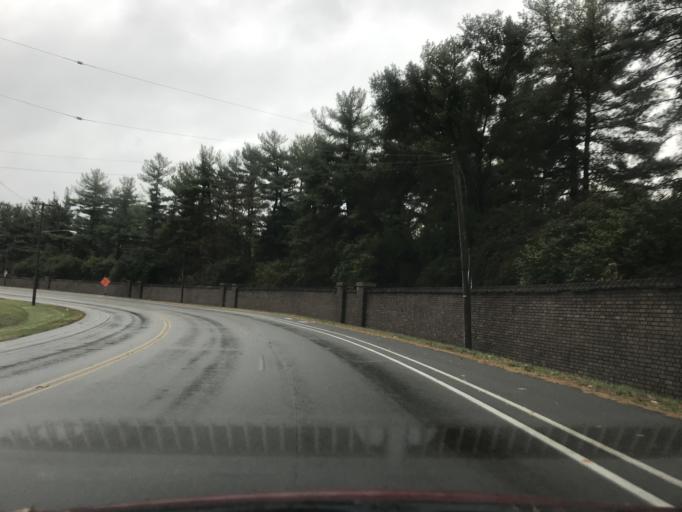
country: US
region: Indiana
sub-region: Clark County
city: Jeffersonville
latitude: 38.2463
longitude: -85.7073
